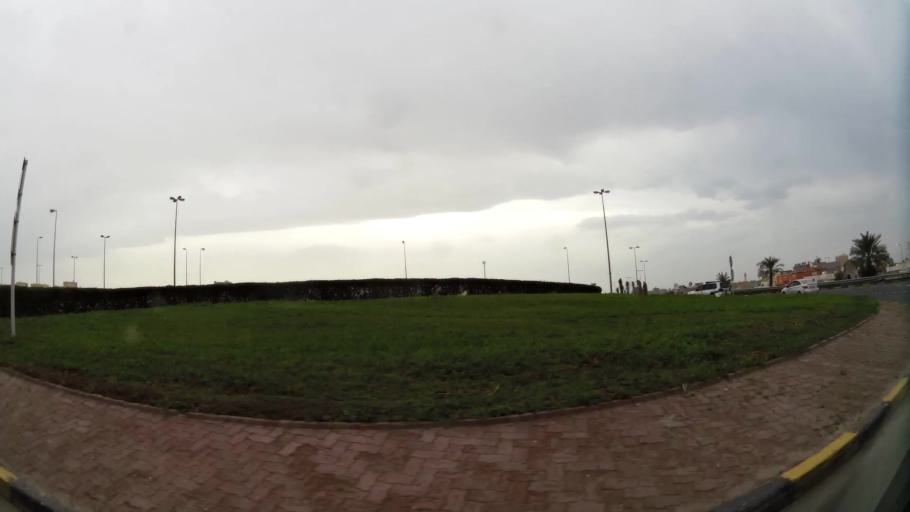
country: BH
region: Central Governorate
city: Dar Kulayb
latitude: 26.0828
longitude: 50.5072
